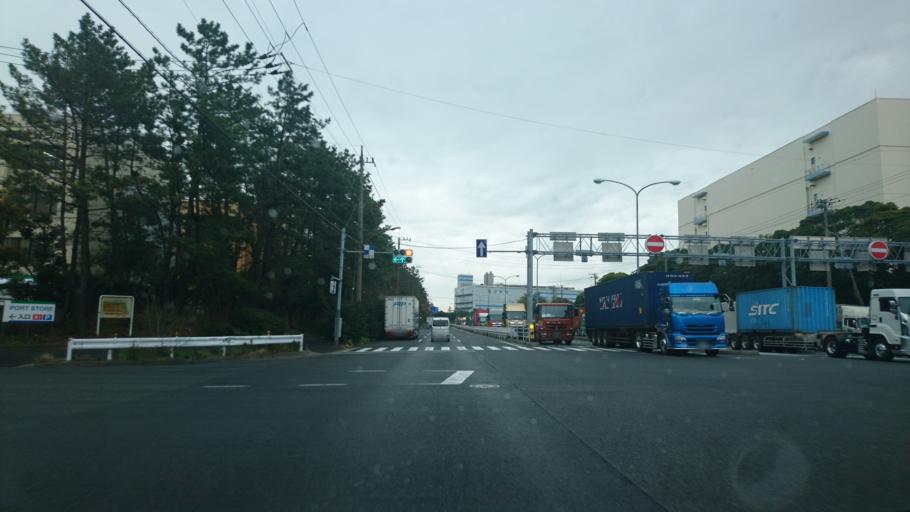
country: JP
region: Kanagawa
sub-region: Kawasaki-shi
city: Kawasaki
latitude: 35.5910
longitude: 139.7683
